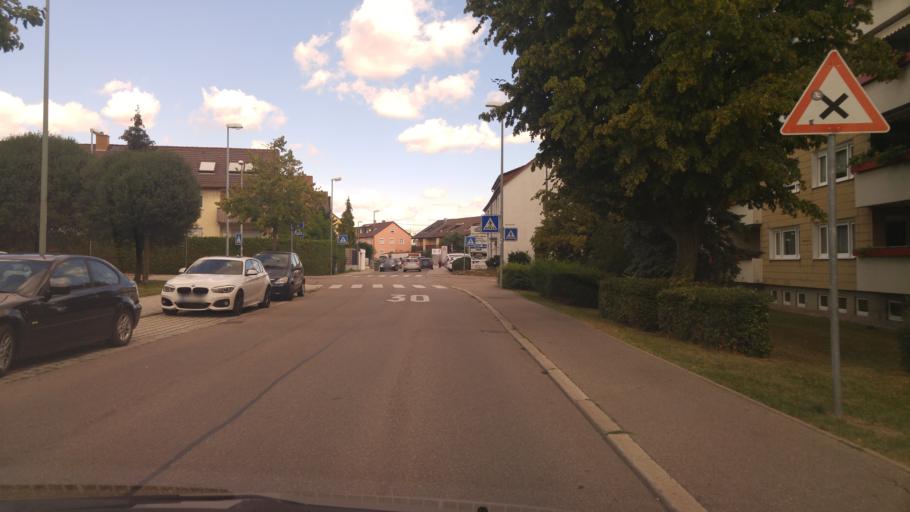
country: DE
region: Baden-Wuerttemberg
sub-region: Regierungsbezirk Stuttgart
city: Gerlingen
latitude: 48.8016
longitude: 9.0668
